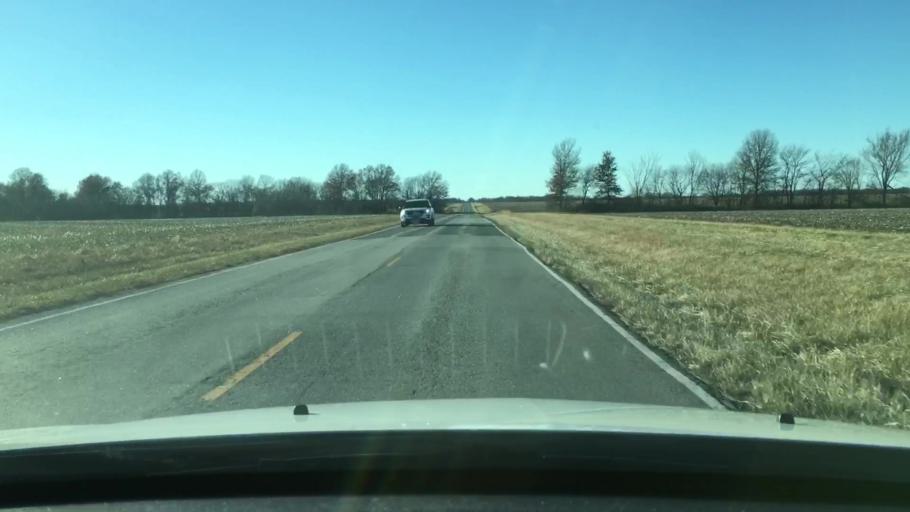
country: US
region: Missouri
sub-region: Audrain County
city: Vandalia
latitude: 39.2814
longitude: -91.6851
